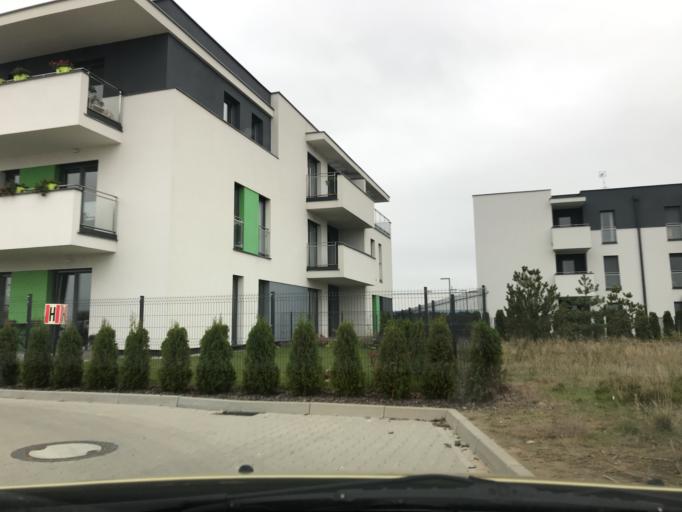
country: PL
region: Greater Poland Voivodeship
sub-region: Powiat poznanski
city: Baranowo
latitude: 52.3955
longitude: 16.7650
